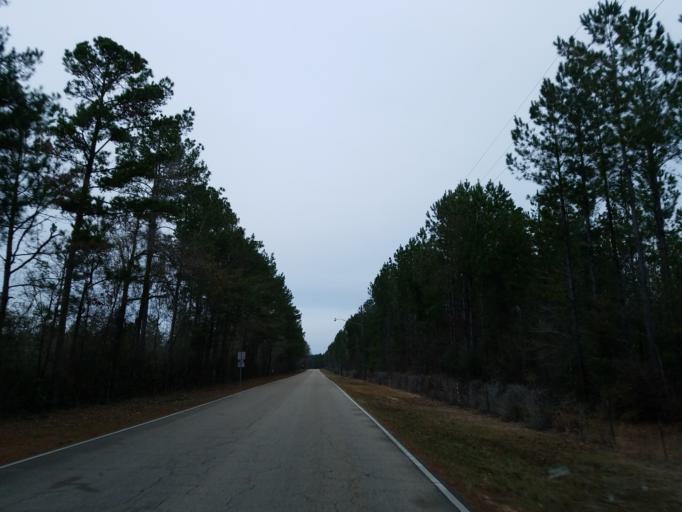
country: US
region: Mississippi
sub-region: Forrest County
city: Hattiesburg
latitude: 31.2741
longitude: -89.2447
